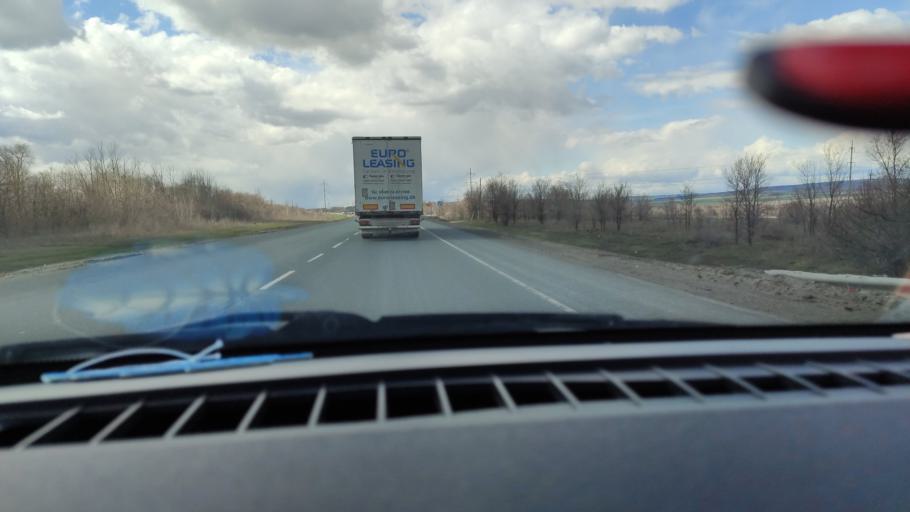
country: RU
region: Samara
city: Varlamovo
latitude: 53.1946
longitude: 48.3252
